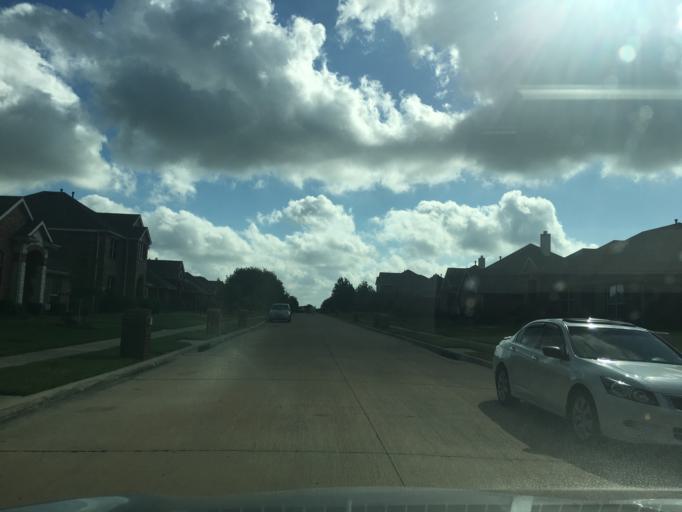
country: US
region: Texas
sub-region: Dallas County
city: Sachse
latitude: 32.9640
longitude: -96.5816
